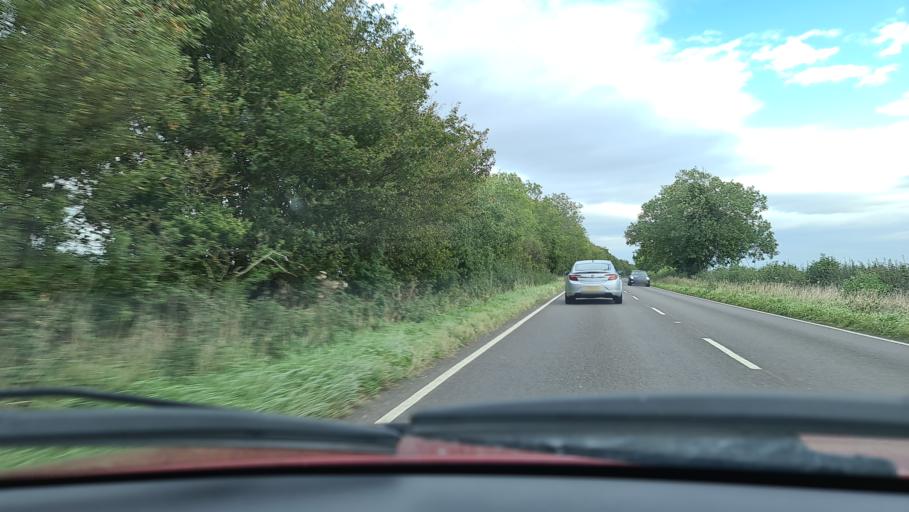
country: GB
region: England
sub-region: Oxfordshire
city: Somerton
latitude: 51.9721
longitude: -1.2277
